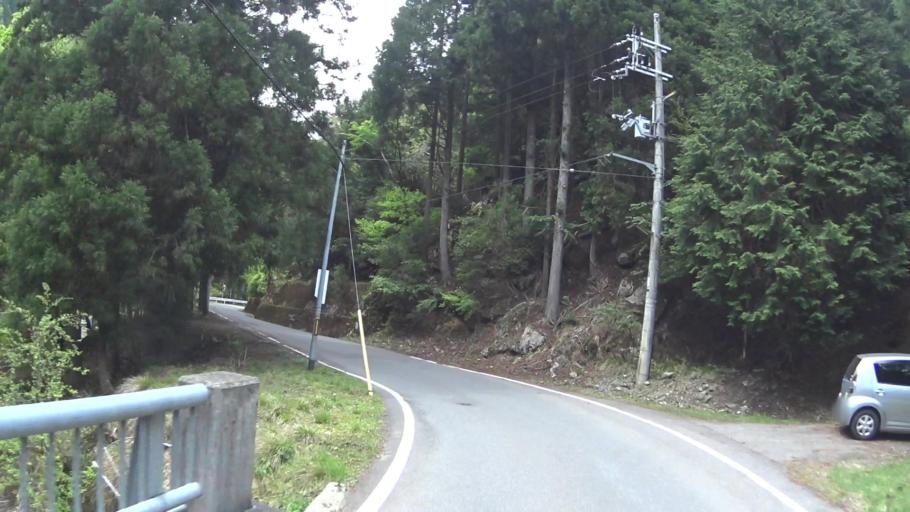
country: JP
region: Shiga Prefecture
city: Kitahama
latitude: 35.2018
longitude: 135.7498
